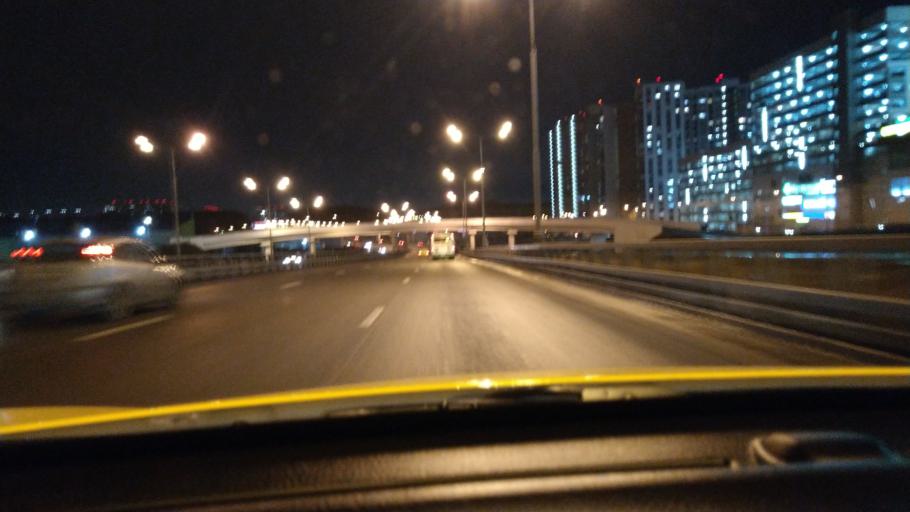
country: RU
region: Moskovskaya
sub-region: Leninskiy Rayon
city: Vnukovo
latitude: 55.6262
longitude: 37.3046
